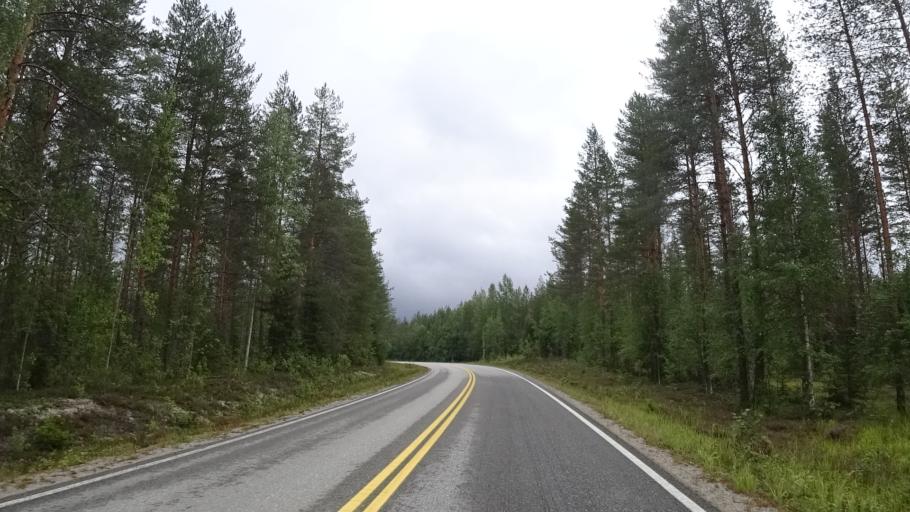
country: FI
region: North Karelia
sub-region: Joensuu
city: Ilomantsi
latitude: 63.2506
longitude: 30.7111
